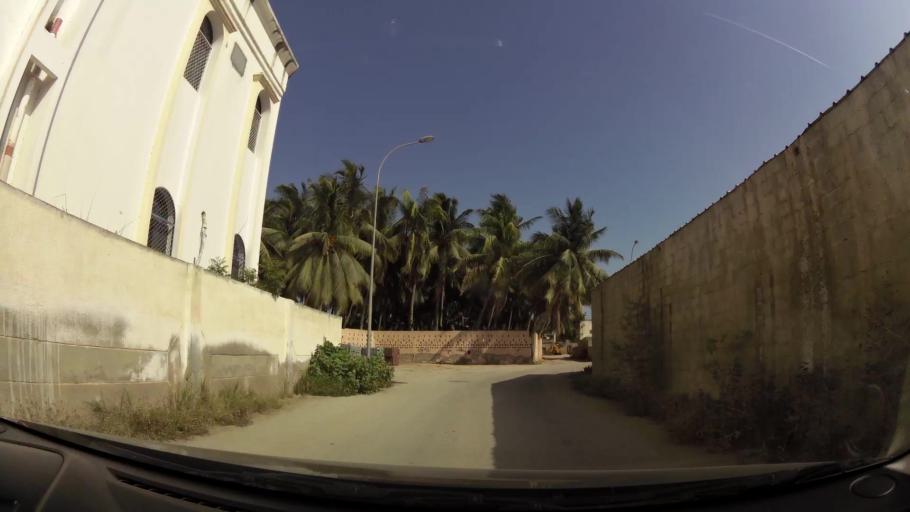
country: OM
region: Zufar
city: Salalah
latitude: 16.9990
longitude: 54.0387
